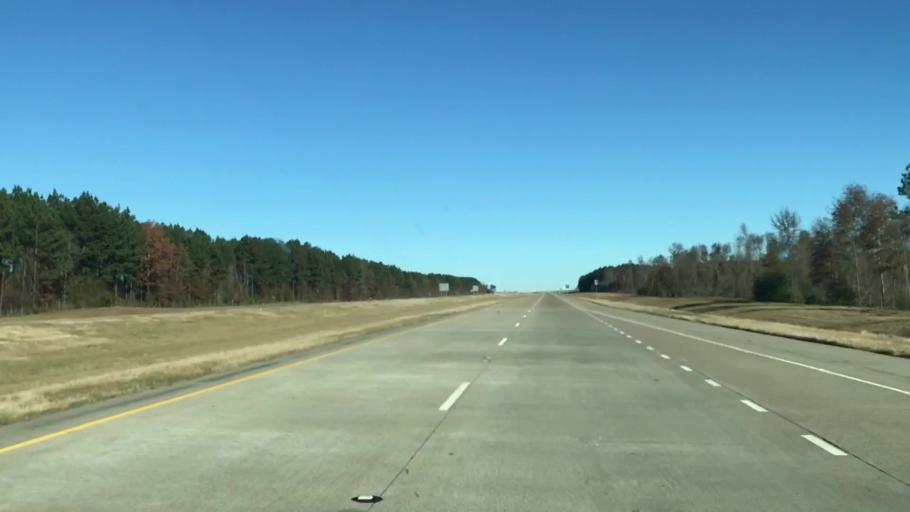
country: US
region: Louisiana
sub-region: Caddo Parish
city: Blanchard
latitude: 32.6028
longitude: -93.8327
